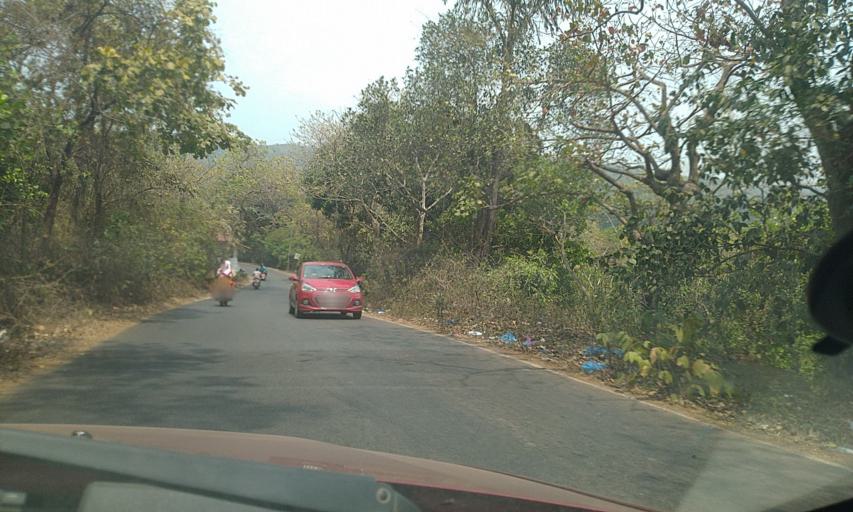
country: IN
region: Goa
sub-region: North Goa
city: Solim
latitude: 15.6147
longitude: 73.7920
